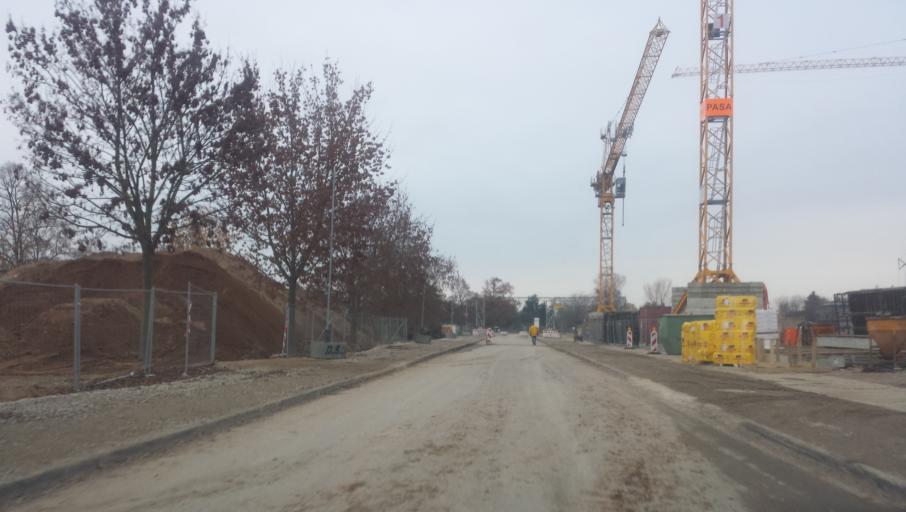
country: DE
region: Hesse
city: Viernheim
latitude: 49.5213
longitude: 8.5308
